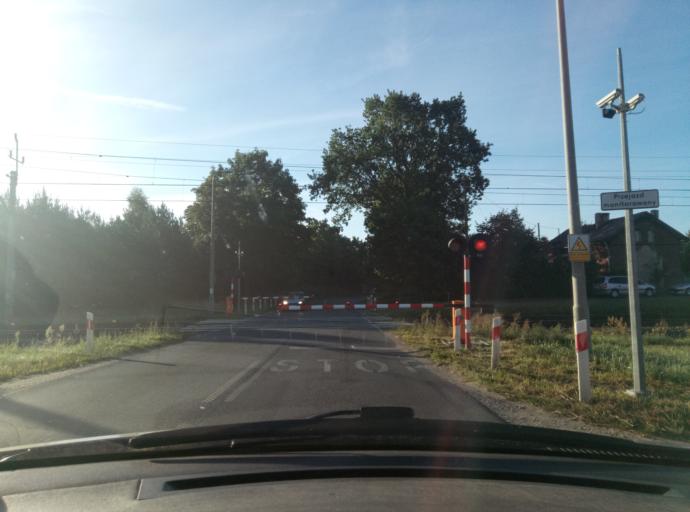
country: PL
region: Kujawsko-Pomorskie
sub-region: Powiat wabrzeski
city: Wabrzezno
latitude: 53.2342
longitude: 18.9507
